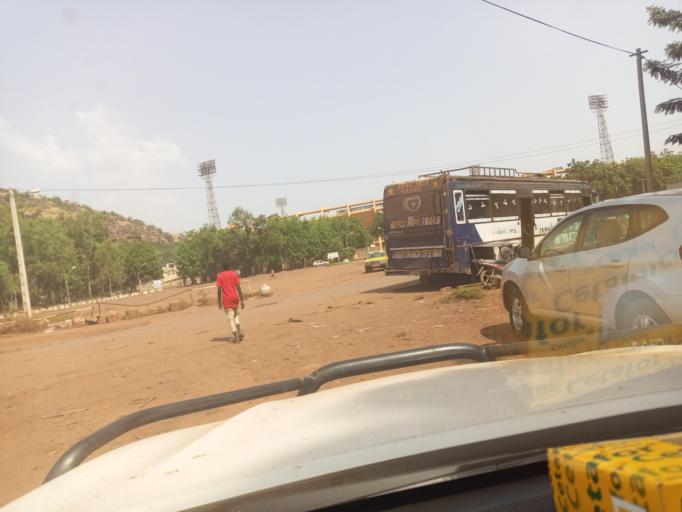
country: ML
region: Bamako
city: Bamako
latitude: 12.6598
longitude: -7.9957
